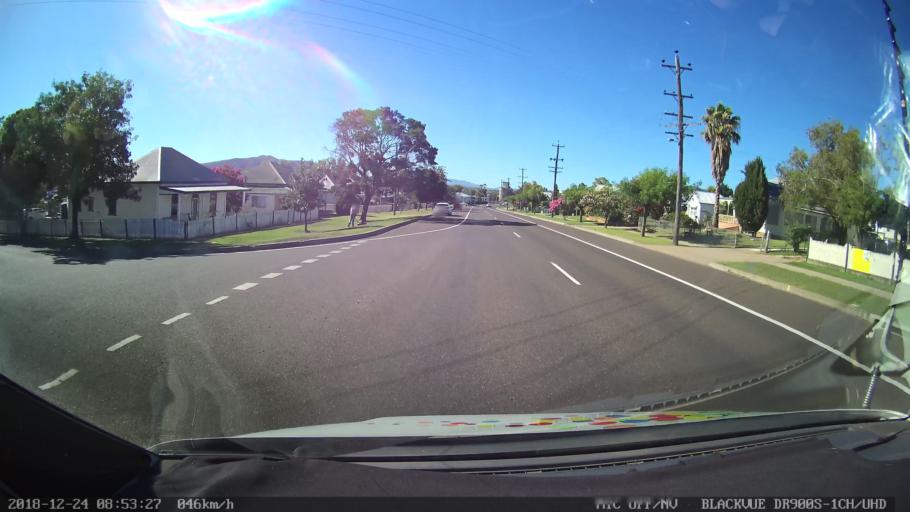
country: AU
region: New South Wales
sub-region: Liverpool Plains
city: Quirindi
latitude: -31.4986
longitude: 150.6812
